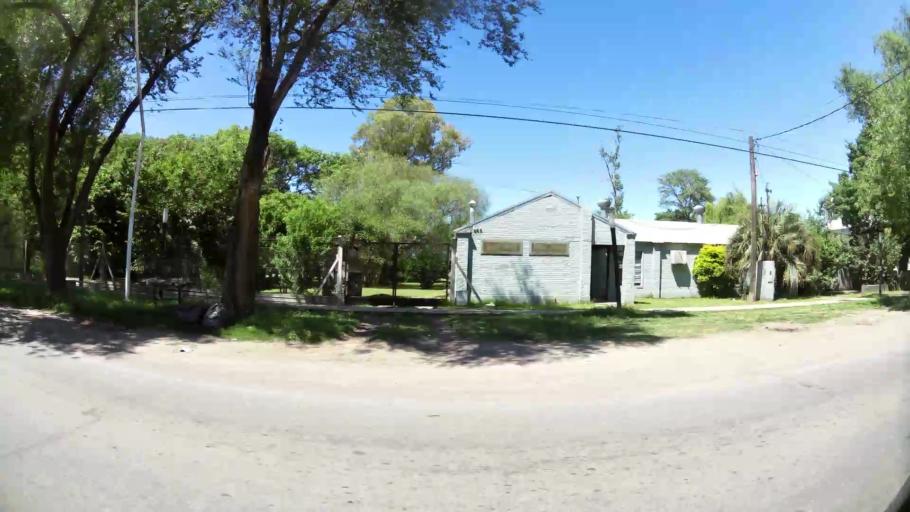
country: AR
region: Santa Fe
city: Esperanza
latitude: -31.4402
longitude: -60.9397
